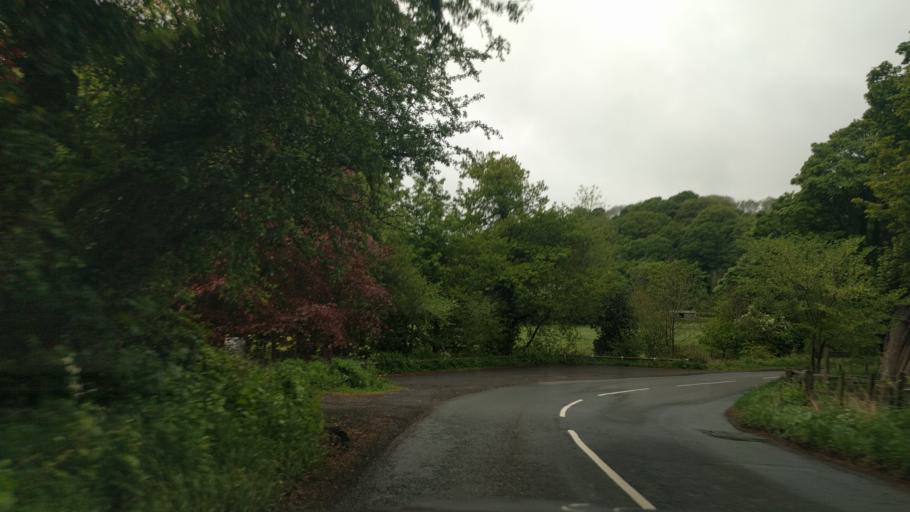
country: GB
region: England
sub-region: Northumberland
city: Morpeth
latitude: 55.1662
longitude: -1.7109
